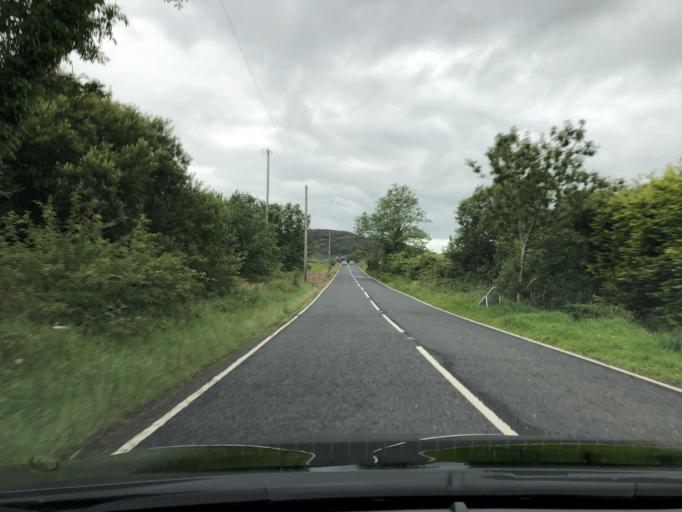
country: GB
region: Northern Ireland
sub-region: Down District
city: Castlewellan
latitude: 54.2581
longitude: -5.9861
